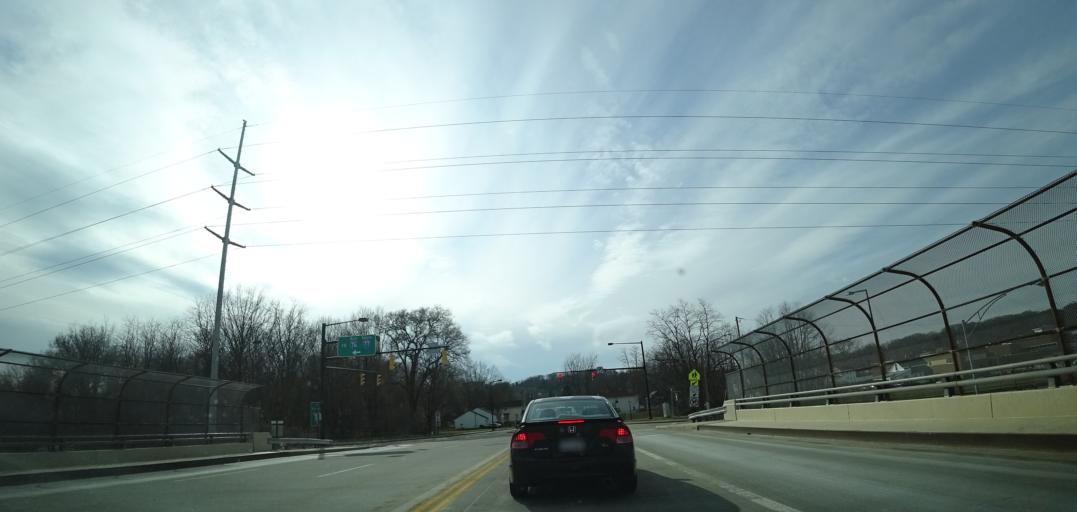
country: US
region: Ohio
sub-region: Summit County
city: Akron
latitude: 41.0706
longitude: -81.5375
